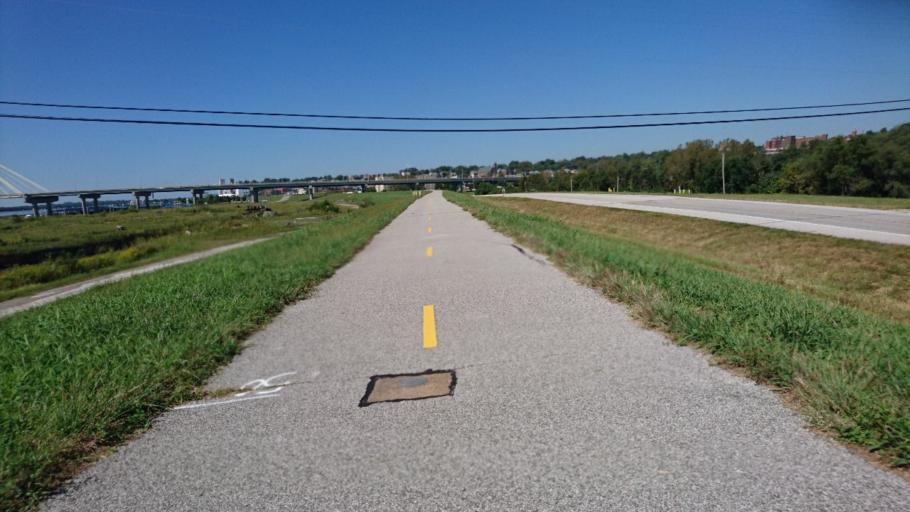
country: US
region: Illinois
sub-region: Madison County
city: Alton
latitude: 38.8826
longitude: -90.1686
